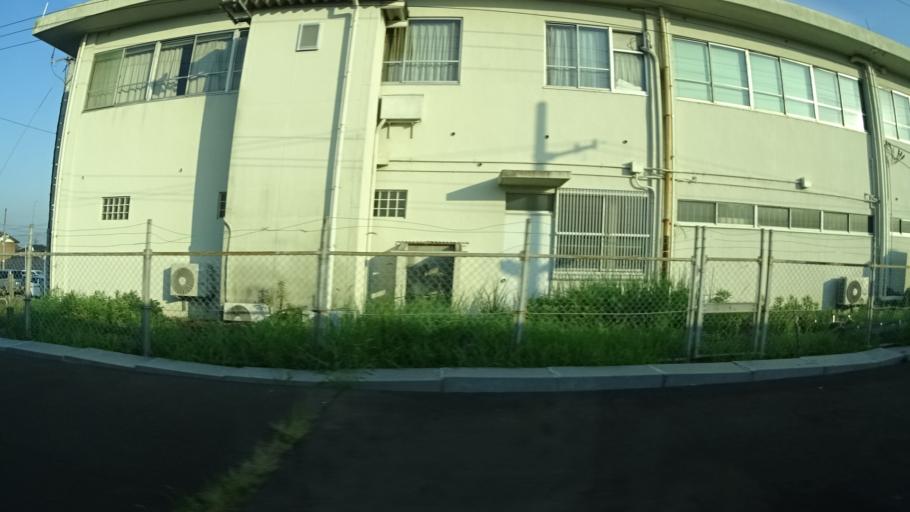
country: JP
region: Ibaraki
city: Tomobe
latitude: 36.3510
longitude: 140.3074
